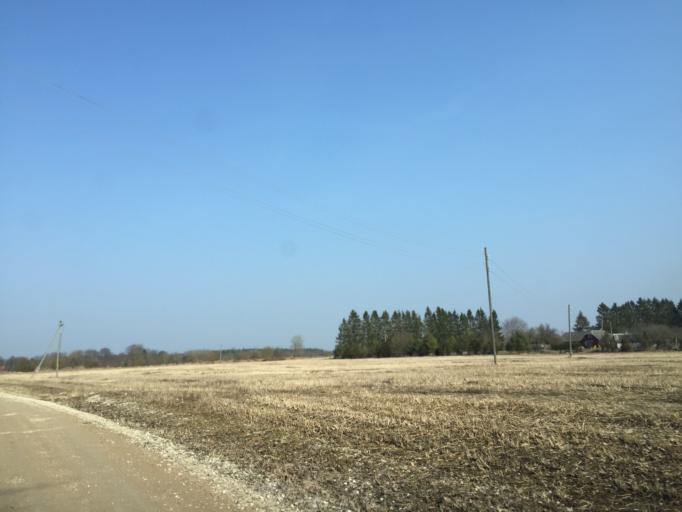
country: EE
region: Saare
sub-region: Kuressaare linn
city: Kuressaare
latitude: 58.3738
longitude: 22.6888
